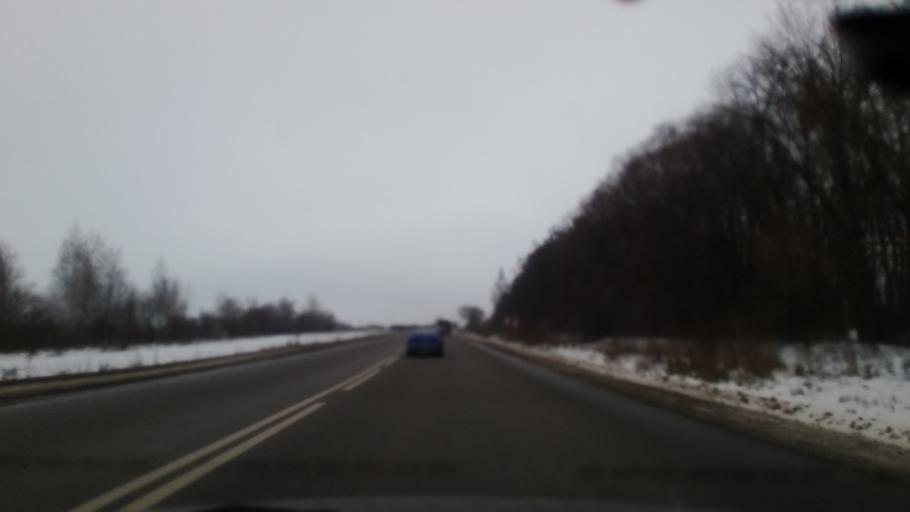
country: RU
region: Tula
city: Borodinskiy
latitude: 54.0304
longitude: 37.8830
